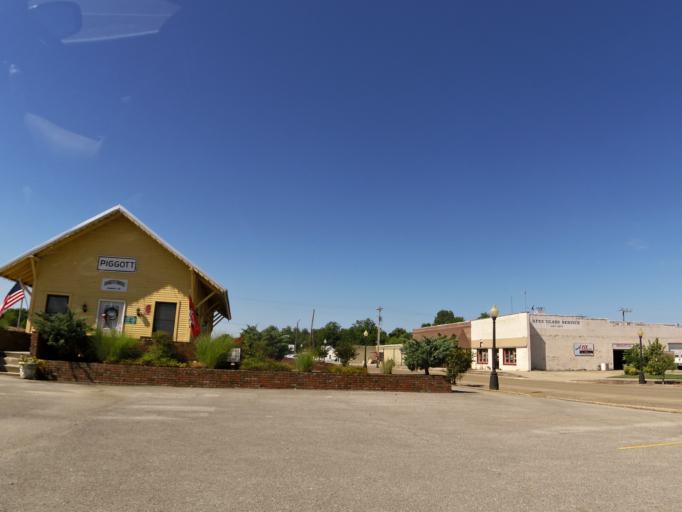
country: US
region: Arkansas
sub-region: Clay County
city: Piggott
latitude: 36.3820
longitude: -90.1905
